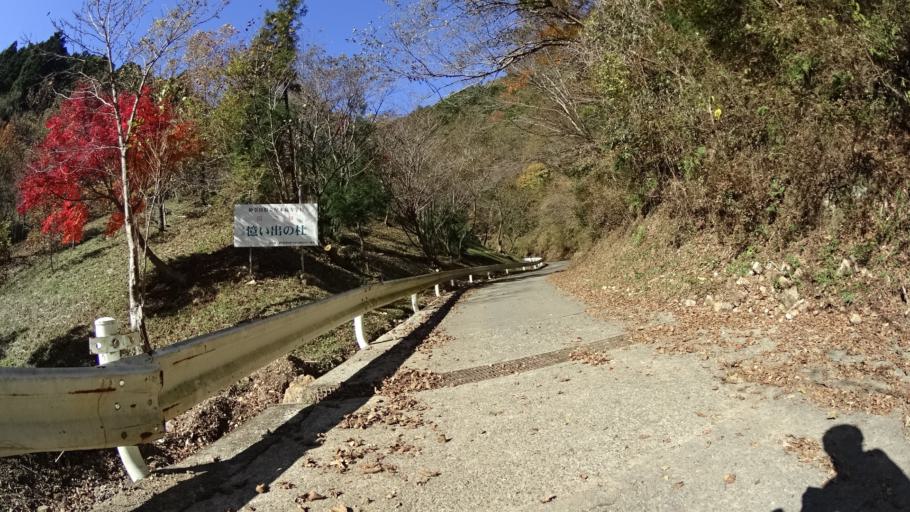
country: JP
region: Kanagawa
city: Atsugi
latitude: 35.5103
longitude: 139.2691
